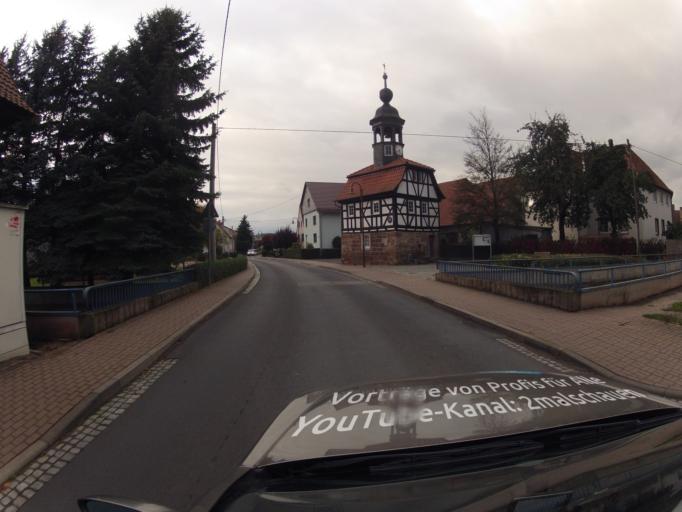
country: DE
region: Thuringia
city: Breitungen
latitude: 50.7623
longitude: 10.3264
